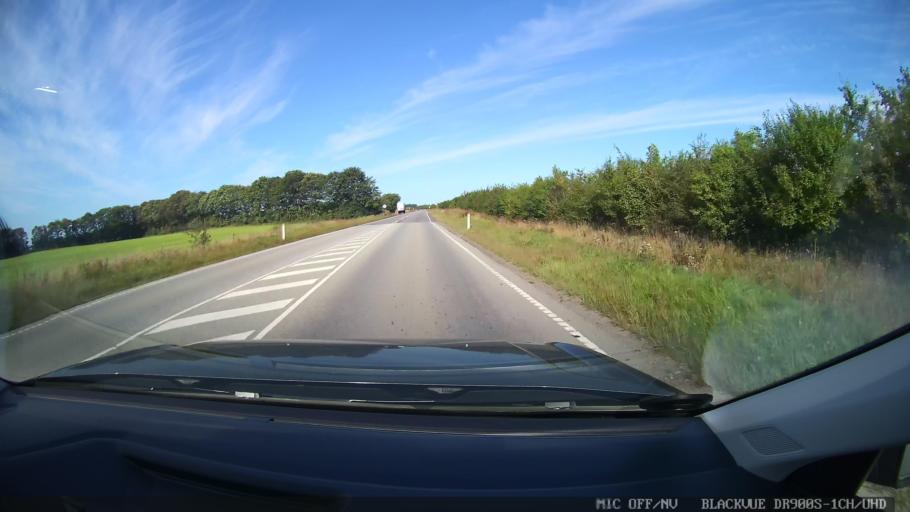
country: DK
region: North Denmark
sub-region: Mariagerfjord Kommune
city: Hobro
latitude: 56.6620
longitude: 9.7797
